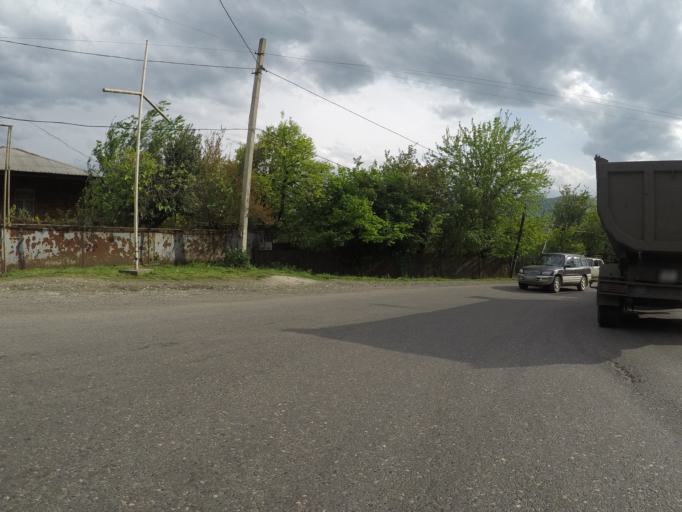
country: GE
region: Imereti
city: Zestap'oni
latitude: 42.1130
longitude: 43.0490
